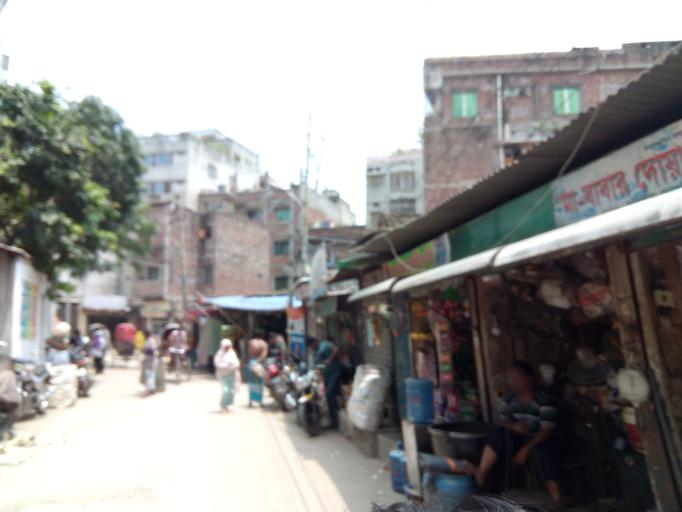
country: BD
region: Dhaka
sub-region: Dhaka
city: Dhaka
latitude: 23.7186
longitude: 90.4040
